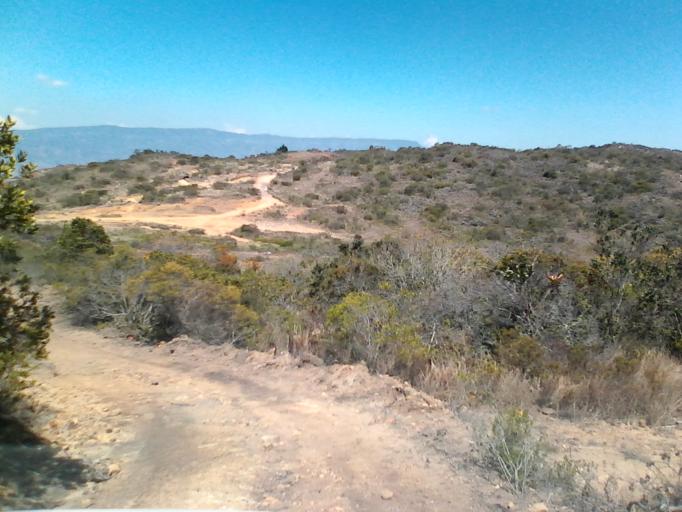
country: CO
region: Boyaca
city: Sachica
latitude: 5.5298
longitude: -73.5462
